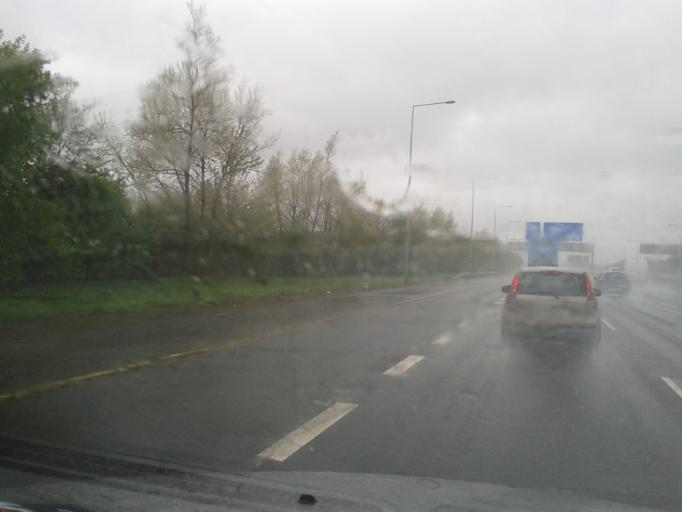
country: IE
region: Leinster
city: Ballymun
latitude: 53.4082
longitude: -6.2836
